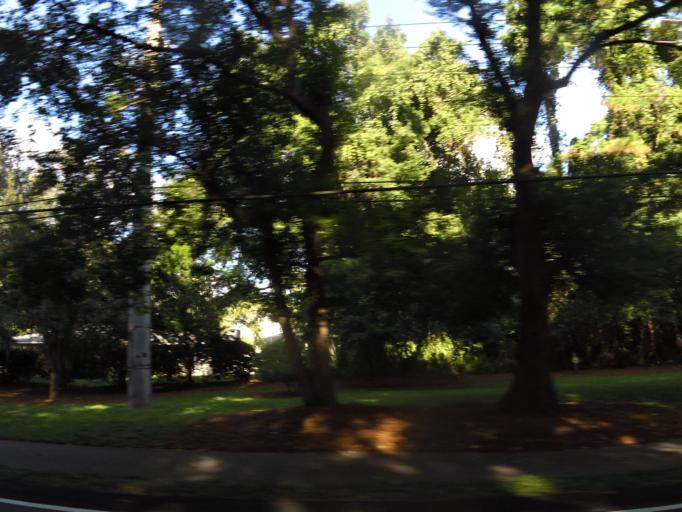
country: US
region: Georgia
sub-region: Glynn County
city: Saint Simon Mills
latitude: 31.2123
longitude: -81.3755
